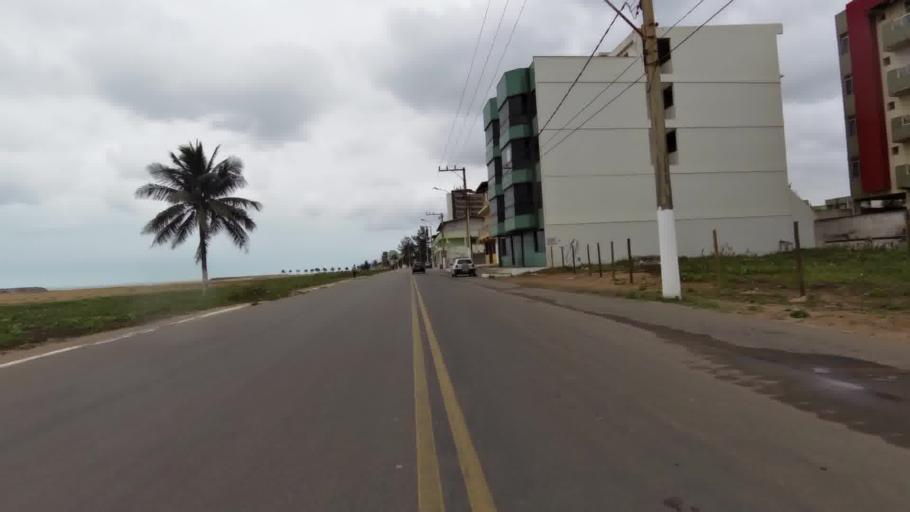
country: BR
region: Espirito Santo
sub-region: Marataizes
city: Marataizes
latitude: -21.0513
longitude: -40.8315
